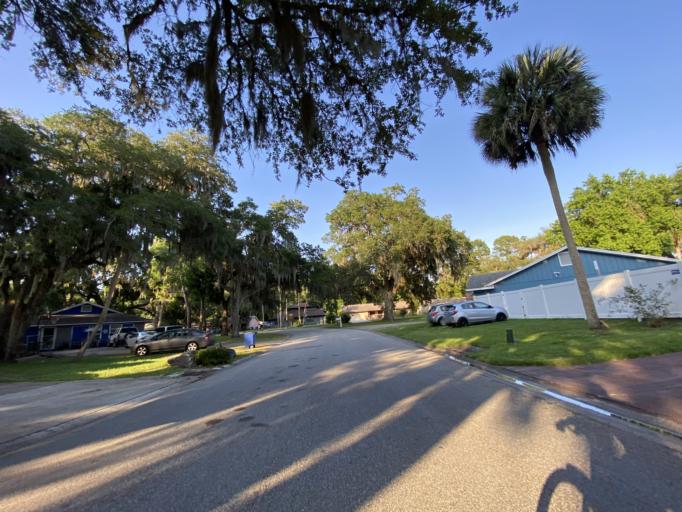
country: US
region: Florida
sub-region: Volusia County
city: Port Orange
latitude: 29.1471
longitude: -81.0054
